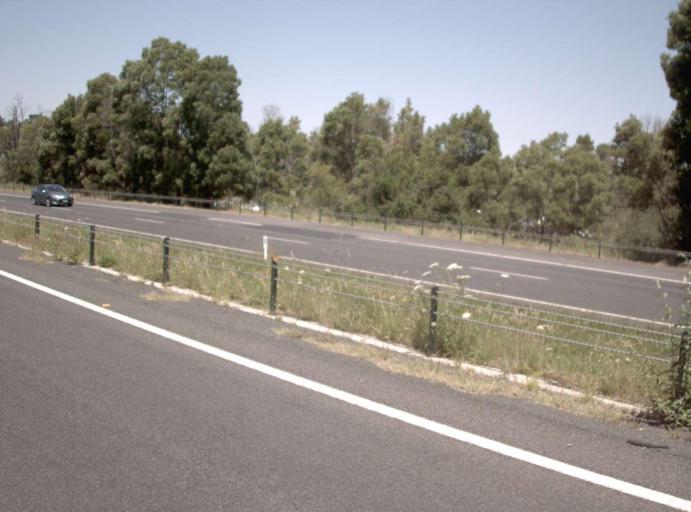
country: AU
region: Victoria
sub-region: Baw Baw
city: Warragul
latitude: -38.1673
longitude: 145.9158
